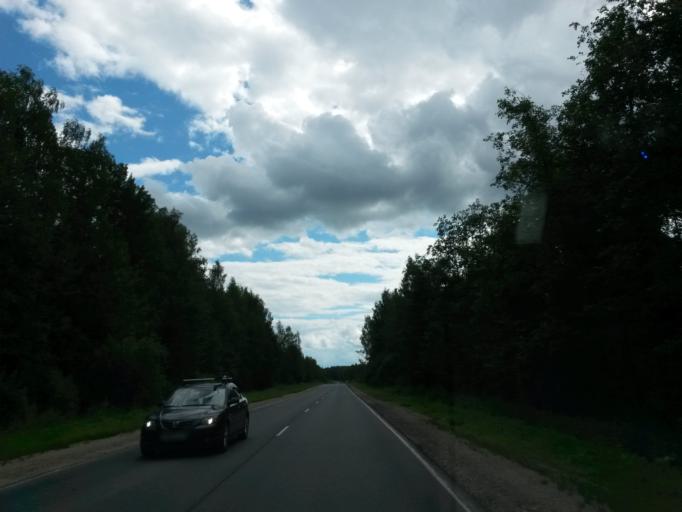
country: RU
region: Ivanovo
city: Pistsovo
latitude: 57.0997
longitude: 40.6560
